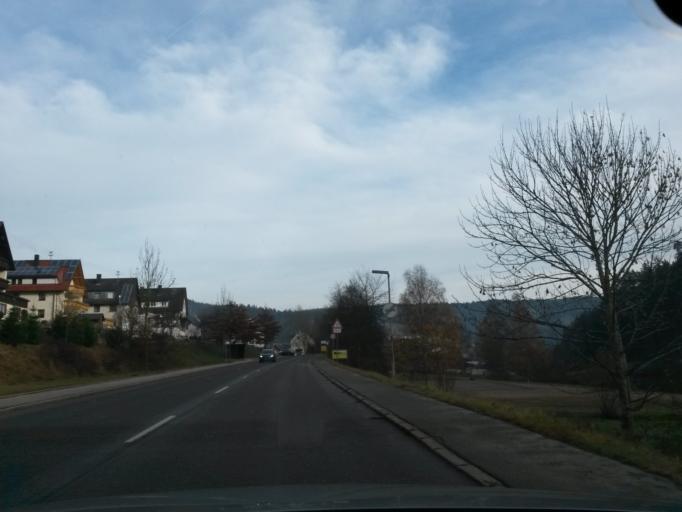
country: DE
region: Baden-Wuerttemberg
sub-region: Freiburg Region
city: Tennenbronn
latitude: 48.1876
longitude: 8.3452
